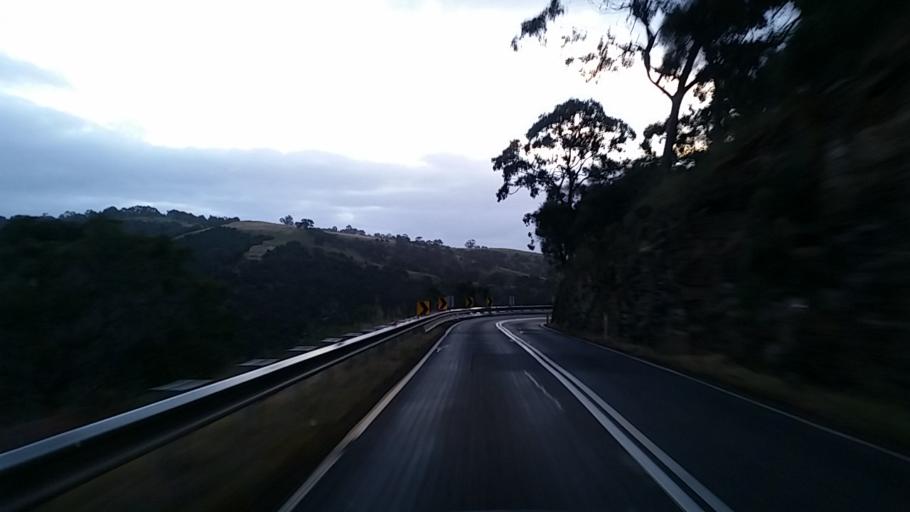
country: AU
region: South Australia
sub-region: Burnside
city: Beaumont
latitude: -34.9488
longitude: 138.6735
